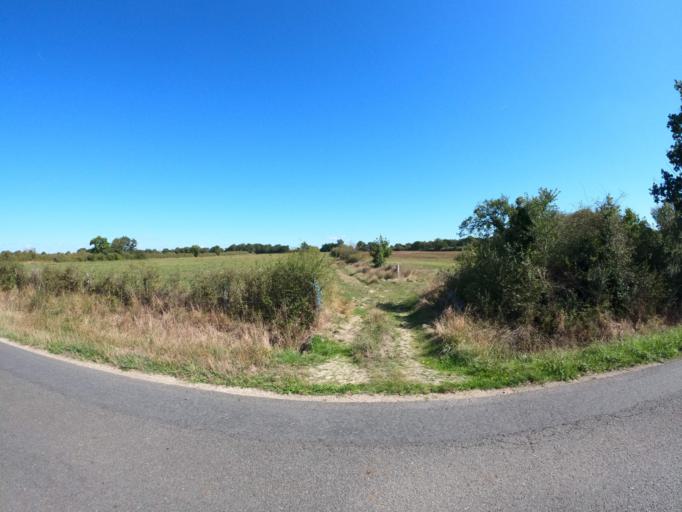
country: FR
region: Poitou-Charentes
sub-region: Departement de la Vienne
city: Lathus-Saint-Remy
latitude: 46.3183
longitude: 0.9740
